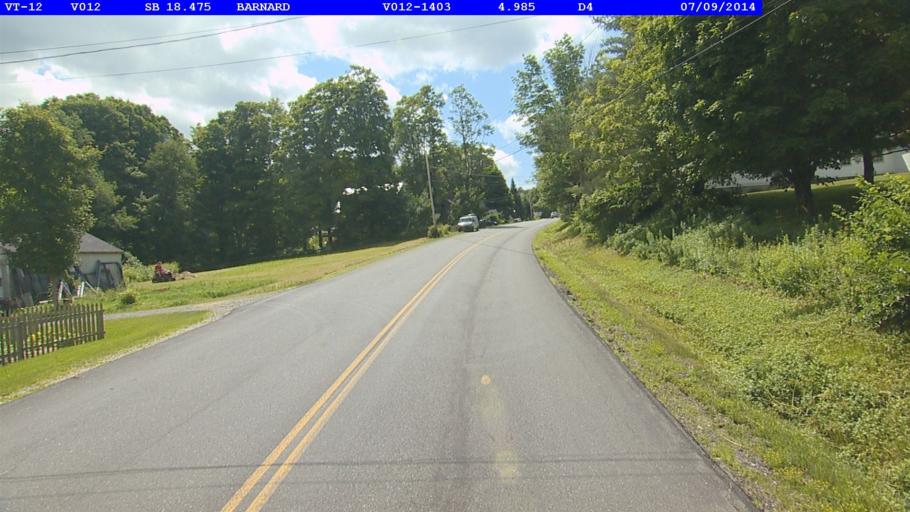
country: US
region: Vermont
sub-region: Windsor County
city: Woodstock
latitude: 43.7313
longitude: -72.6215
